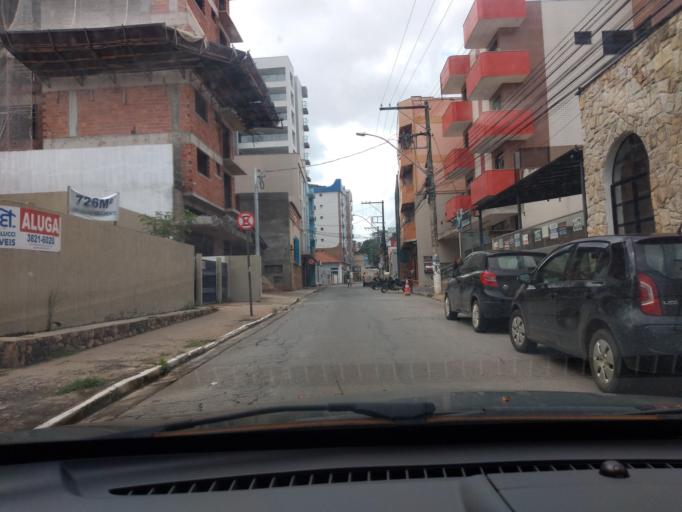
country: BR
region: Minas Gerais
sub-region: Lavras
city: Lavras
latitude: -21.2352
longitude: -44.9978
